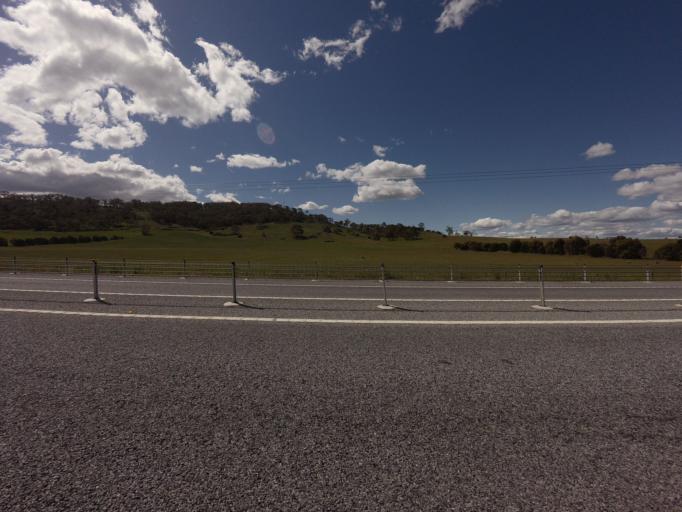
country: AU
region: Tasmania
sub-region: Northern Midlands
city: Evandale
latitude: -42.0678
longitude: 147.4764
